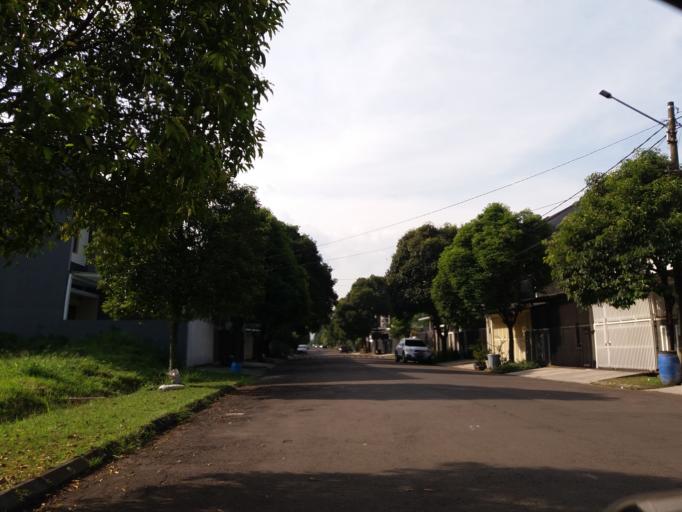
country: ID
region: West Java
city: Pameungpeuk
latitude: -6.9637
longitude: 107.6295
